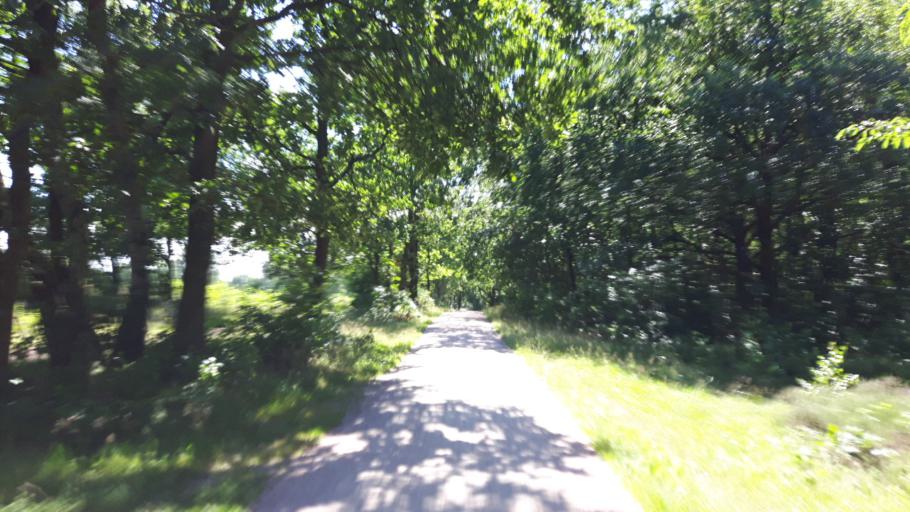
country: NL
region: North Holland
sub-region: Gemeente Wijdemeren
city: Nieuw-Loosdrecht
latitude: 52.2022
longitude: 5.1590
